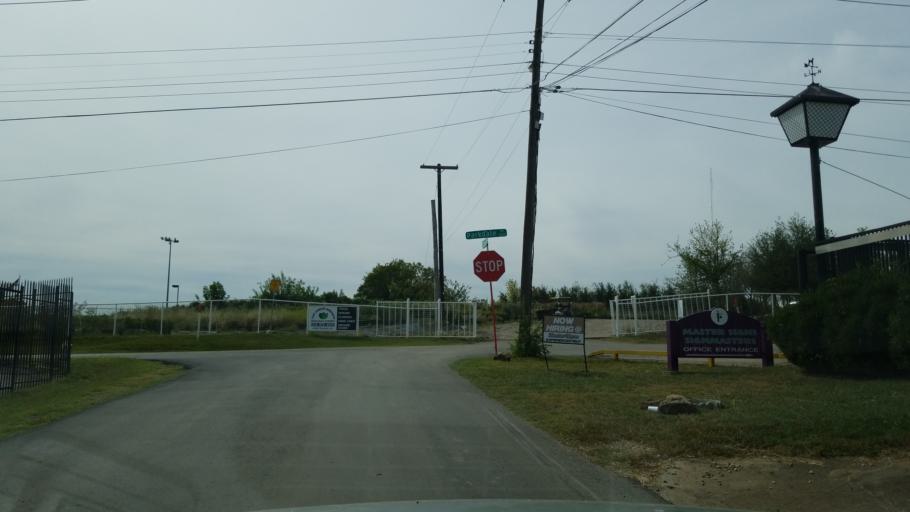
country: US
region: Texas
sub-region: Dallas County
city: Dallas
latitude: 32.7804
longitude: -96.7249
